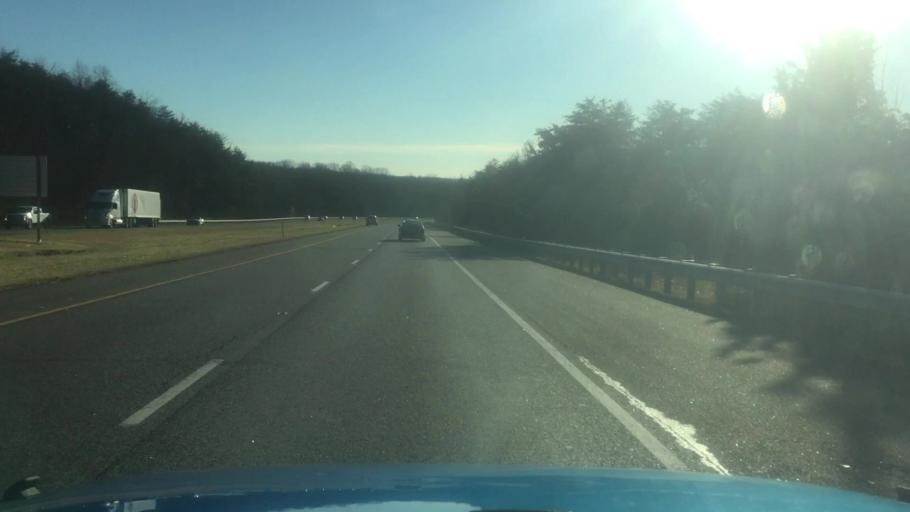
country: US
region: Maryland
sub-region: Prince George's County
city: Berwyn Heights
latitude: 38.9867
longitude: -76.9084
